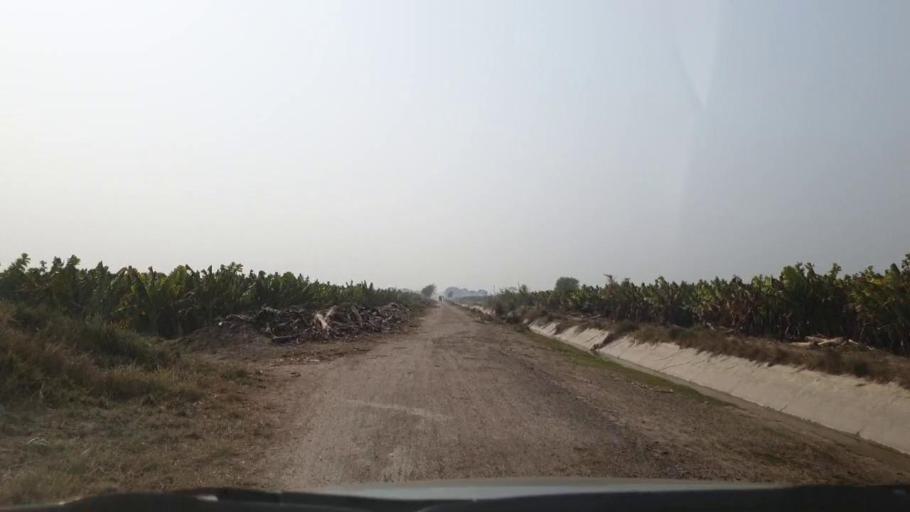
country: PK
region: Sindh
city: Matiari
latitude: 25.6392
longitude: 68.5130
